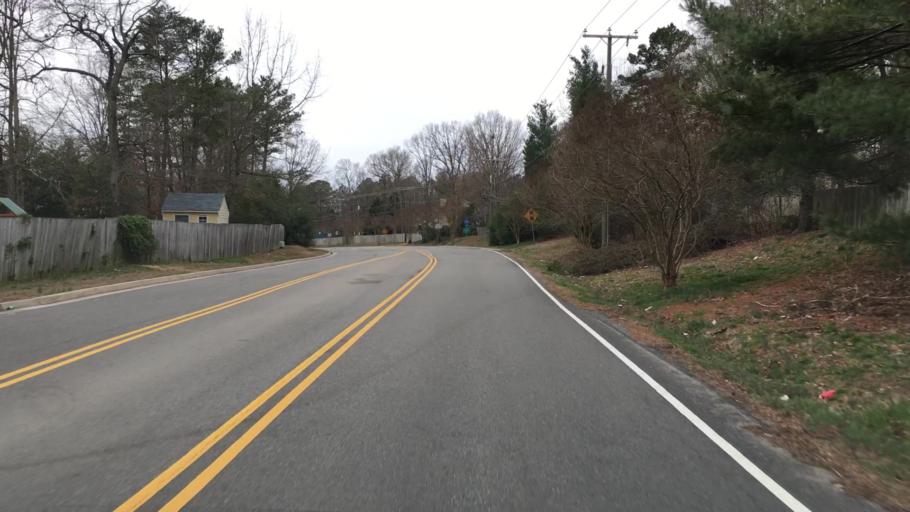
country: US
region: Virginia
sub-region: Henrico County
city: Short Pump
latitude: 37.6651
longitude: -77.5616
